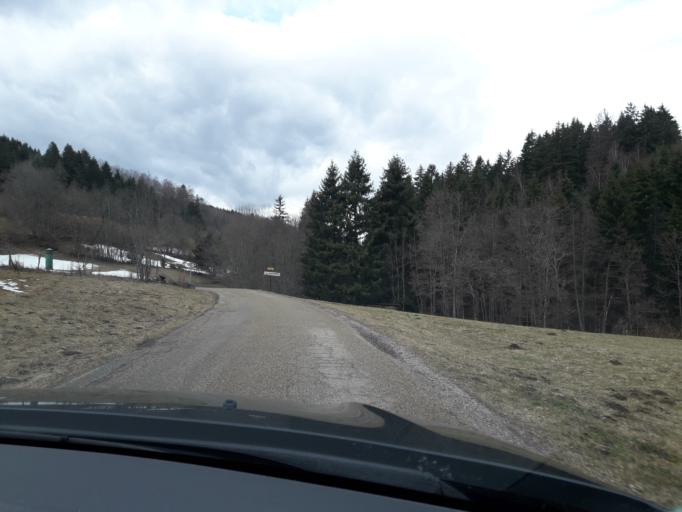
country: FR
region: Rhone-Alpes
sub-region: Departement de l'Isere
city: Le Champ-pres-Froges
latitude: 45.2391
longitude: 5.9711
